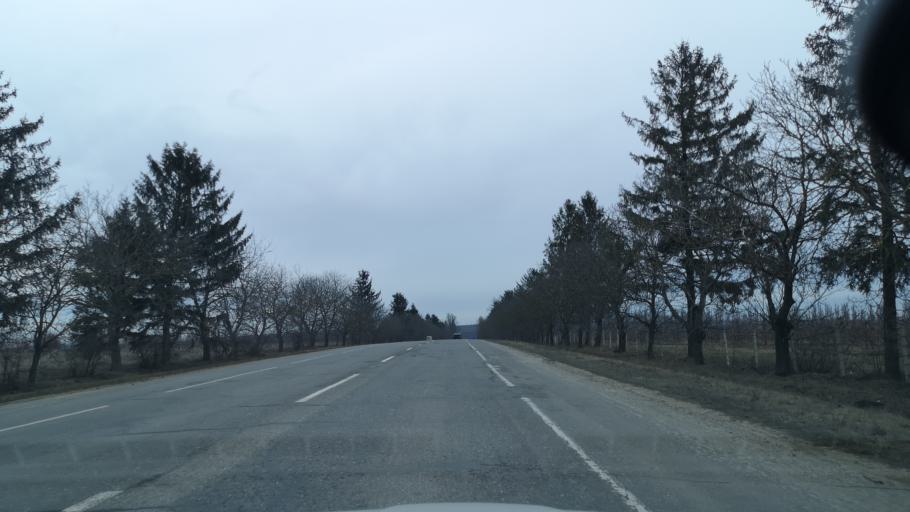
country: MD
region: Briceni
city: Briceni
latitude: 48.3192
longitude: 27.1222
